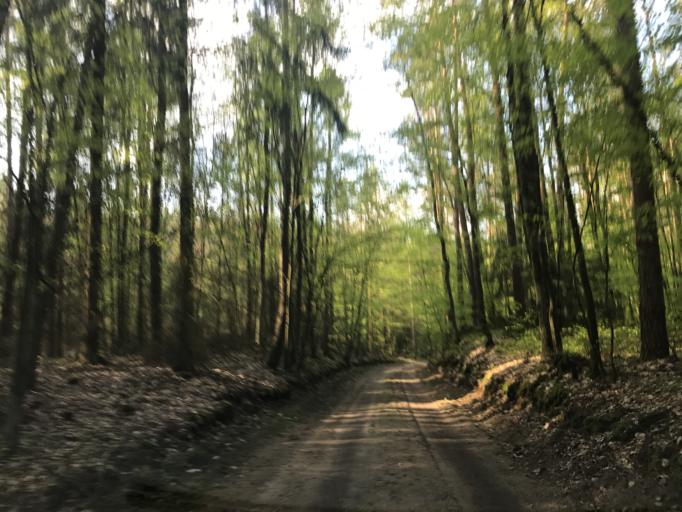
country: PL
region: Kujawsko-Pomorskie
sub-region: Powiat brodnicki
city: Gorzno
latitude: 53.2209
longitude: 19.7018
